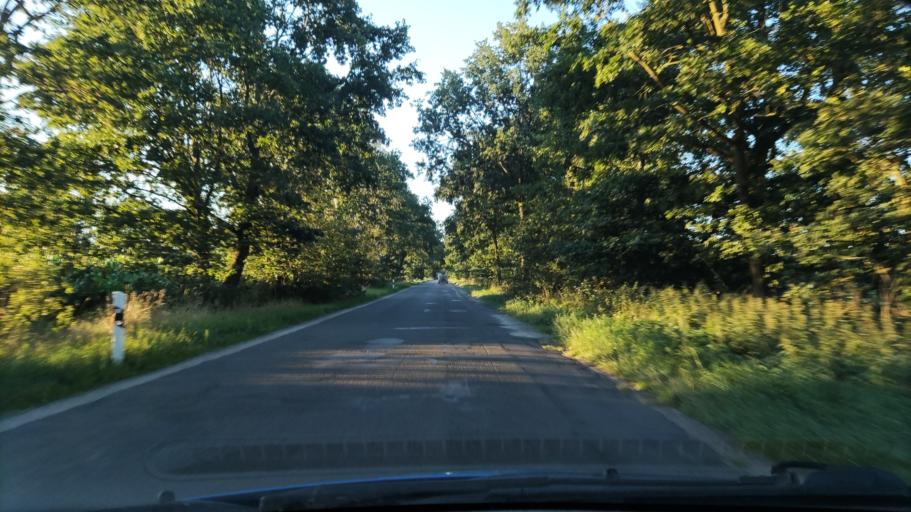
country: DE
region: Lower Saxony
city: Klein Gusborn
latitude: 53.0765
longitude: 11.1926
